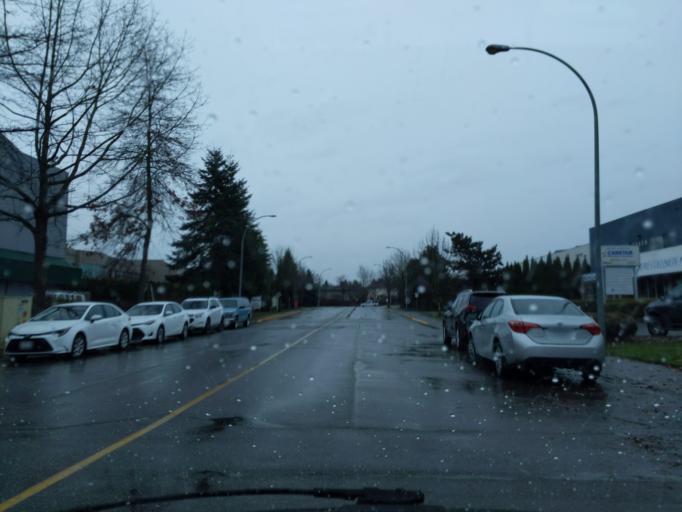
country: CA
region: British Columbia
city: Walnut Grove
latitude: 49.1708
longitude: -122.6653
